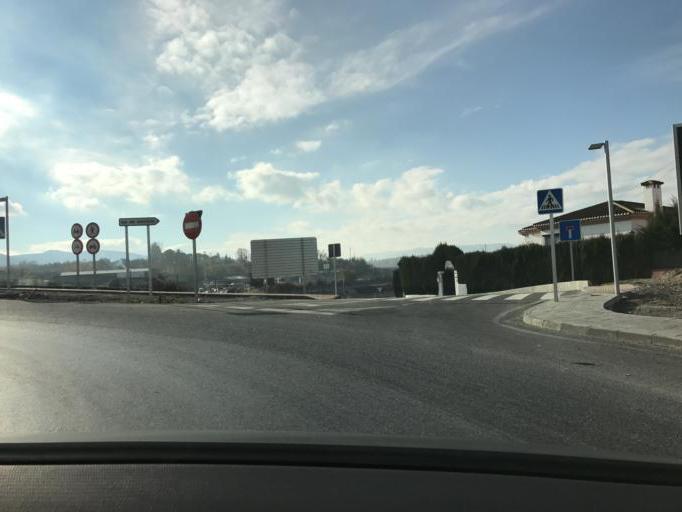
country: ES
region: Andalusia
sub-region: Provincia de Granada
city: Alhendin
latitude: 37.1042
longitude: -3.6396
